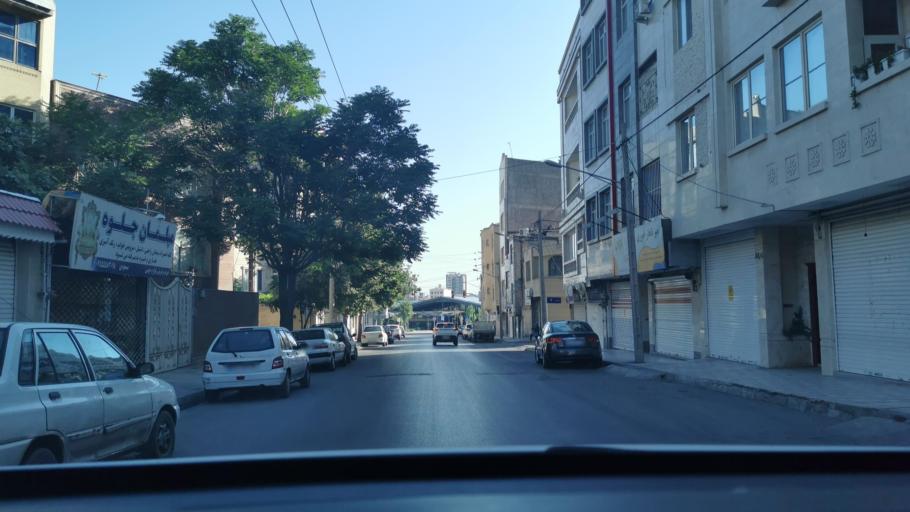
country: IR
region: Razavi Khorasan
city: Mashhad
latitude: 36.3088
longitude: 59.5112
